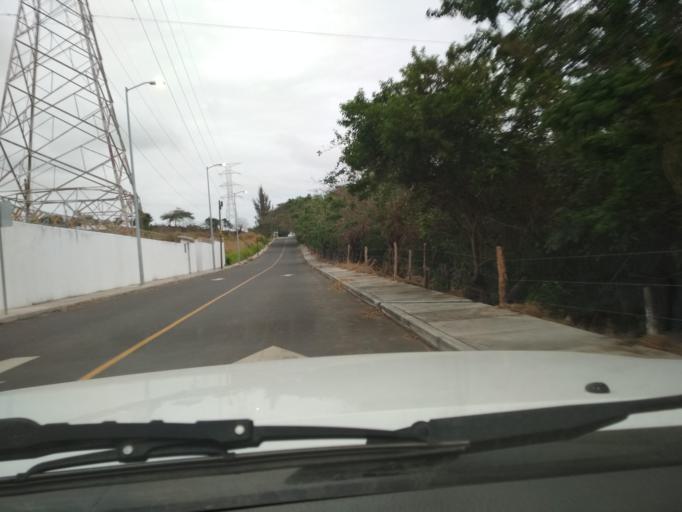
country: MX
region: Veracruz
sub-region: Medellin
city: Fraccionamiento Arboledas San Ramon
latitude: 19.0823
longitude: -96.1369
